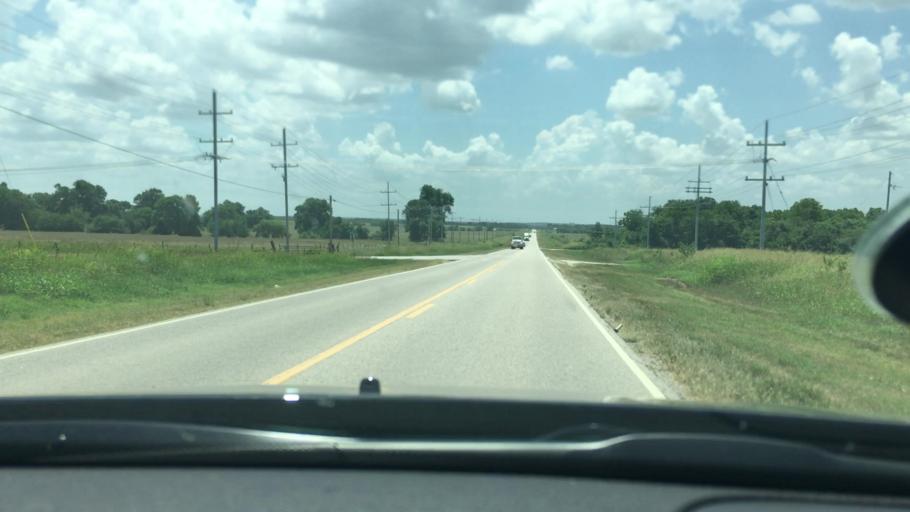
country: US
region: Oklahoma
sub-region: Pontotoc County
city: Ada
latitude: 34.6517
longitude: -96.6349
